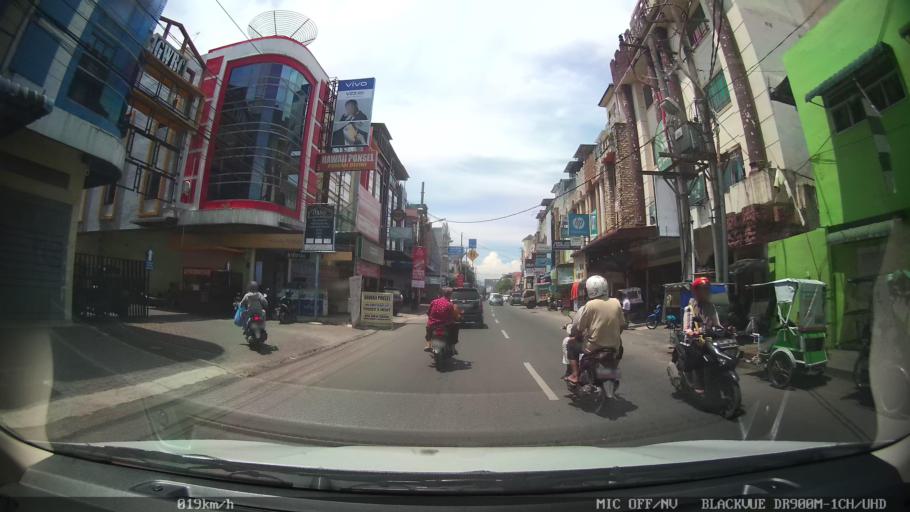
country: ID
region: North Sumatra
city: Binjai
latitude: 3.6040
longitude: 98.4872
